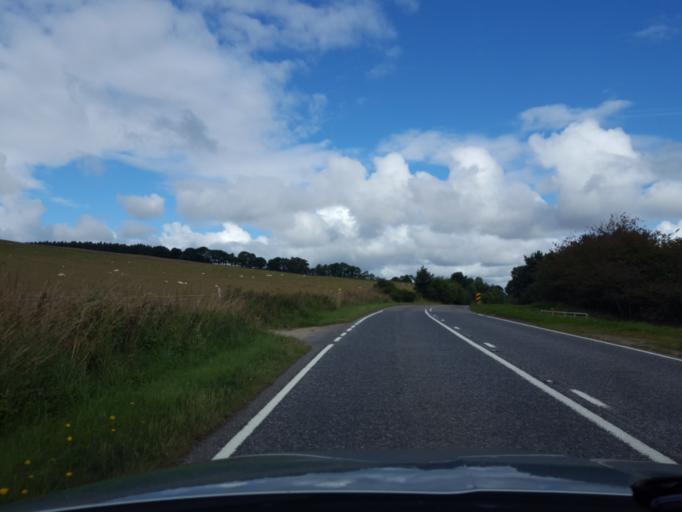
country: GB
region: Scotland
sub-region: Moray
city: Rothes
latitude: 57.5371
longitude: -3.2258
